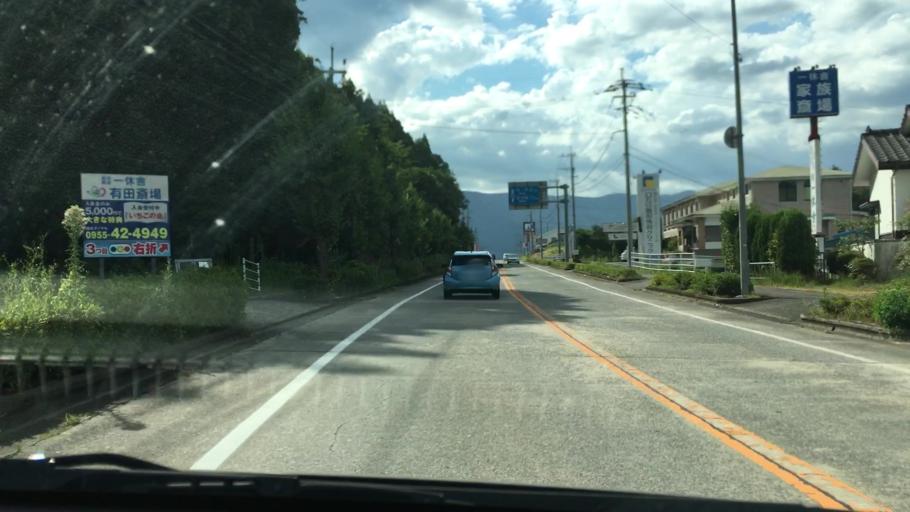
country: JP
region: Saga Prefecture
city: Imaricho-ko
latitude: 33.1824
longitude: 129.8761
